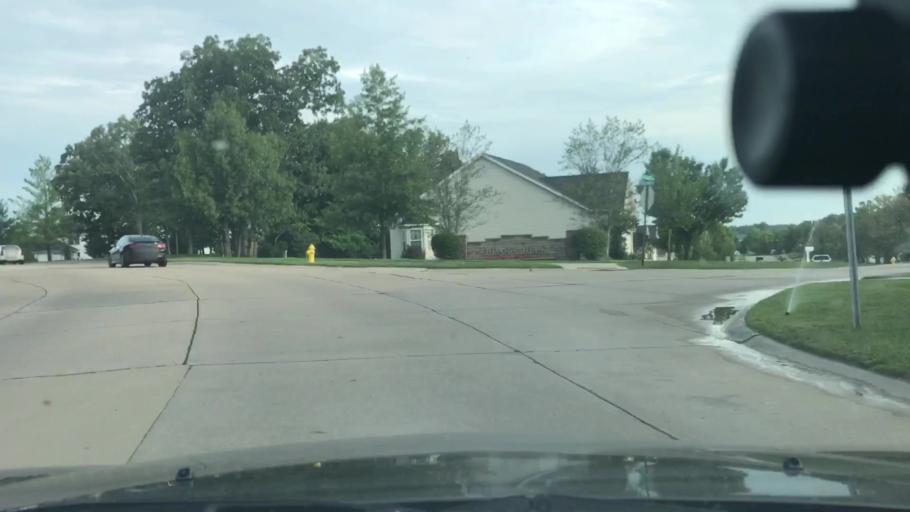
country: US
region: Missouri
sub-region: Saint Charles County
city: Wentzville
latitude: 38.8135
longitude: -90.8881
